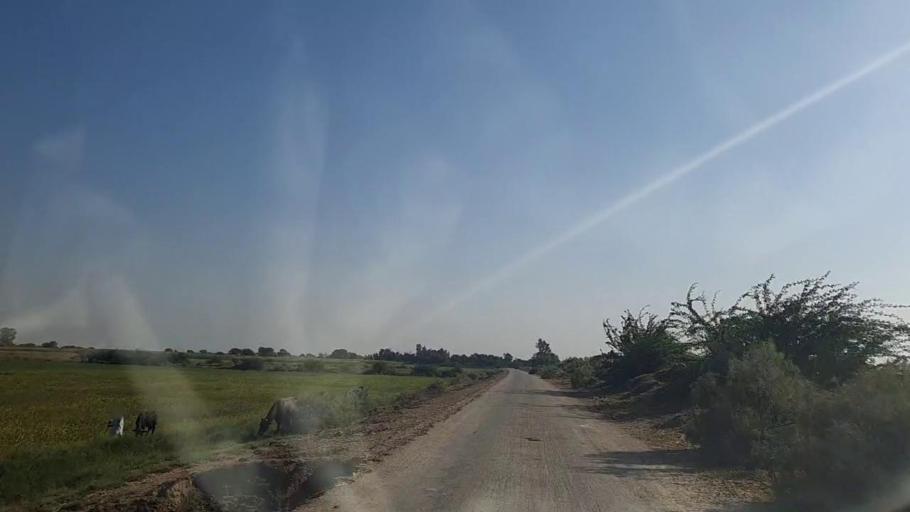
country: PK
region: Sindh
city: Mirpur Batoro
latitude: 24.5571
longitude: 68.1714
